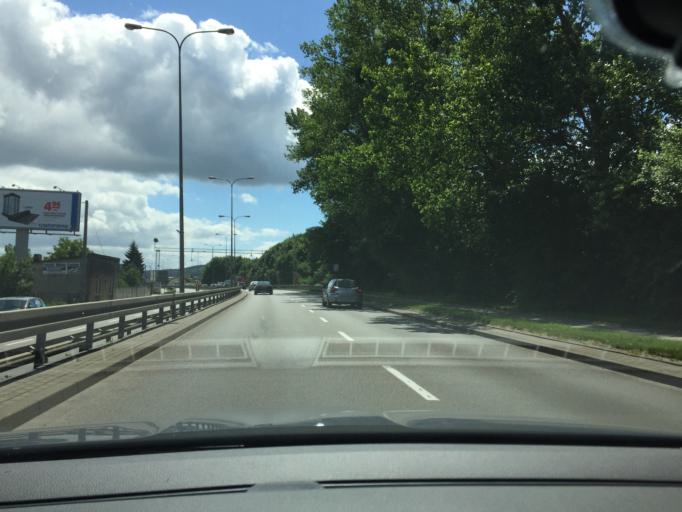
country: PL
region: Pomeranian Voivodeship
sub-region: Powiat wejherowski
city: Reda
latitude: 54.5926
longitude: 18.3561
